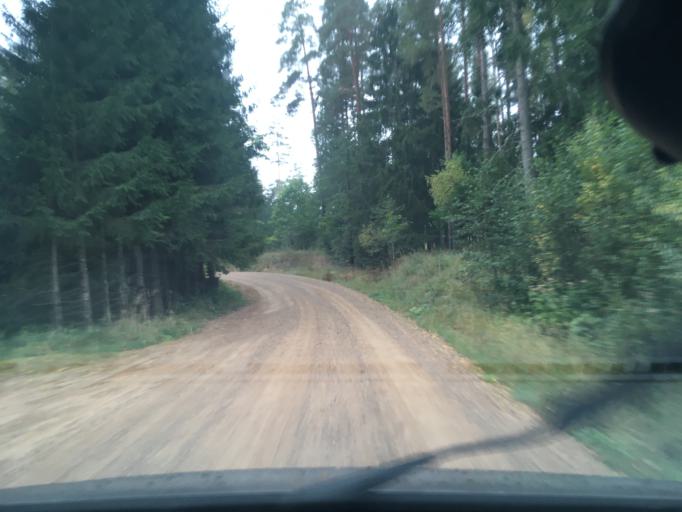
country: LV
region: Kuldigas Rajons
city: Kuldiga
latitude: 57.0192
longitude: 21.9862
